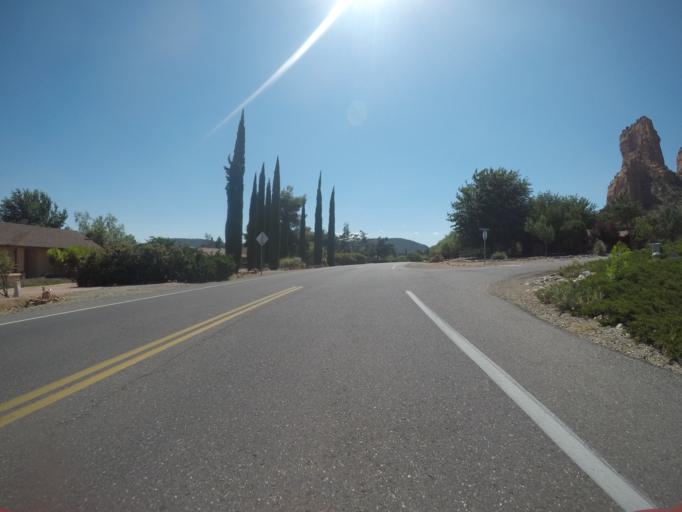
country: US
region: Arizona
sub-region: Yavapai County
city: Village of Oak Creek (Big Park)
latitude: 34.7872
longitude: -111.7683
